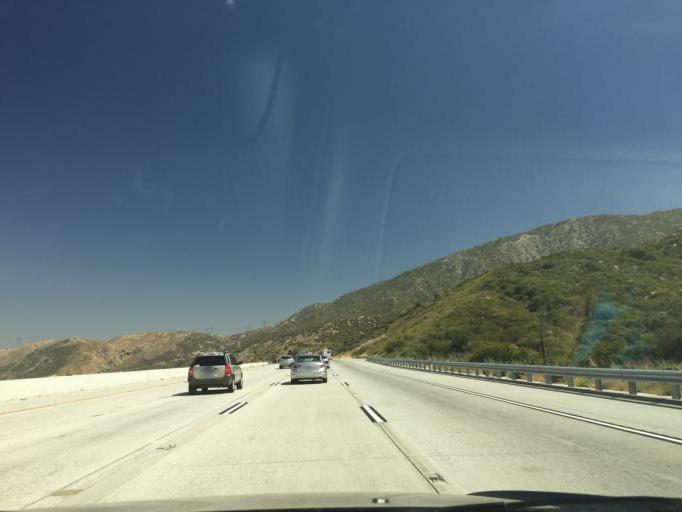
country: US
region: California
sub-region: San Bernardino County
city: Oak Hills
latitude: 34.2861
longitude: -117.4516
